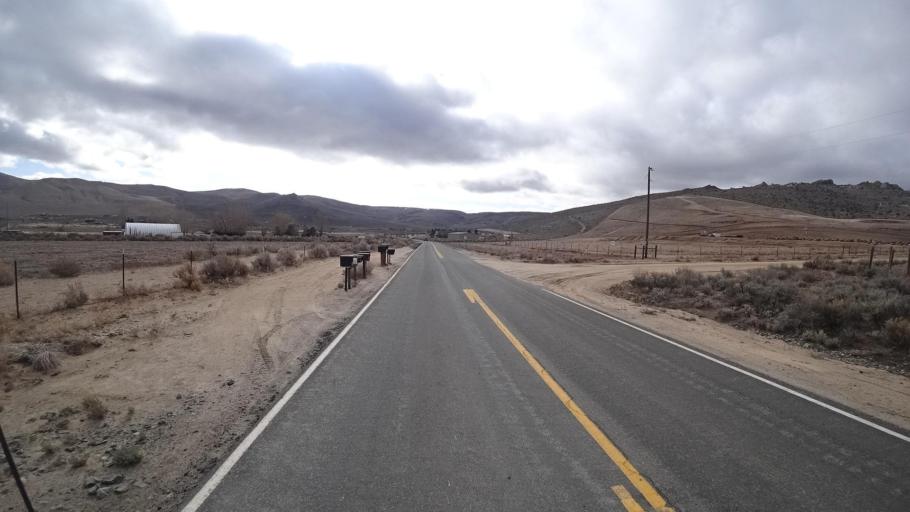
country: US
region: Nevada
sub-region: Washoe County
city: Cold Springs
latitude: 39.8642
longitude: -119.9422
